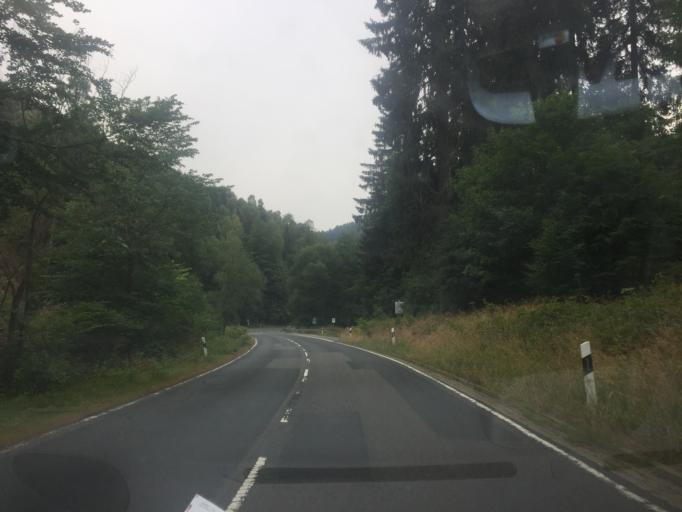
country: DE
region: Lower Saxony
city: Wieda
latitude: 51.6551
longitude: 10.5847
